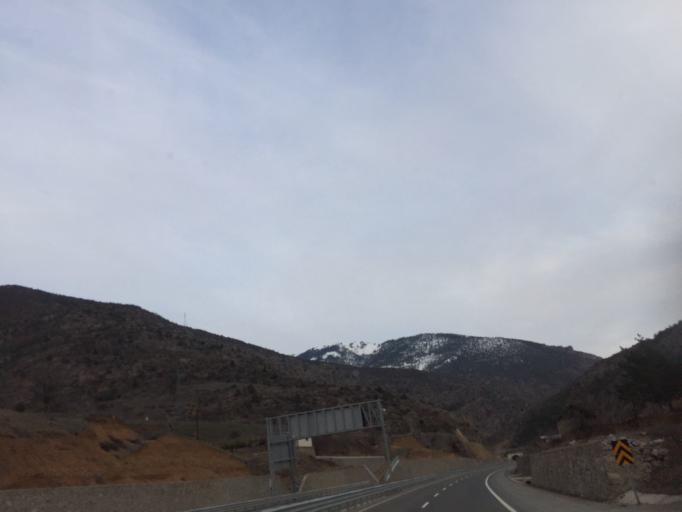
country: TR
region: Gumushane
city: Torul
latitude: 40.5505
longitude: 39.3114
